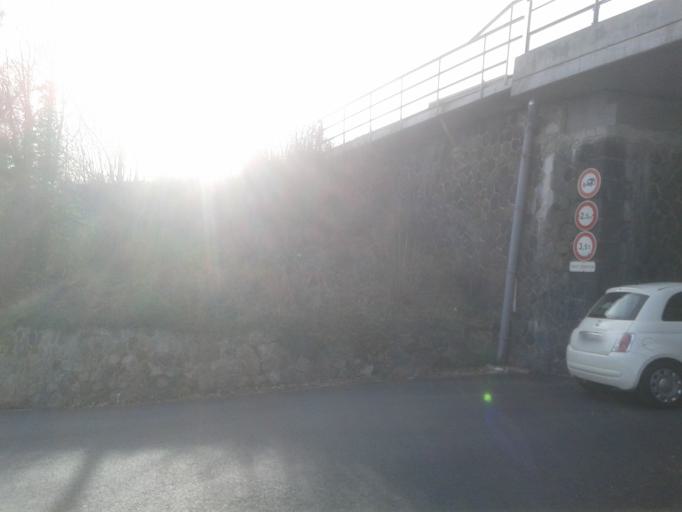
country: FR
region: Auvergne
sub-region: Departement du Puy-de-Dome
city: Chamalieres
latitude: 45.7655
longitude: 3.0705
